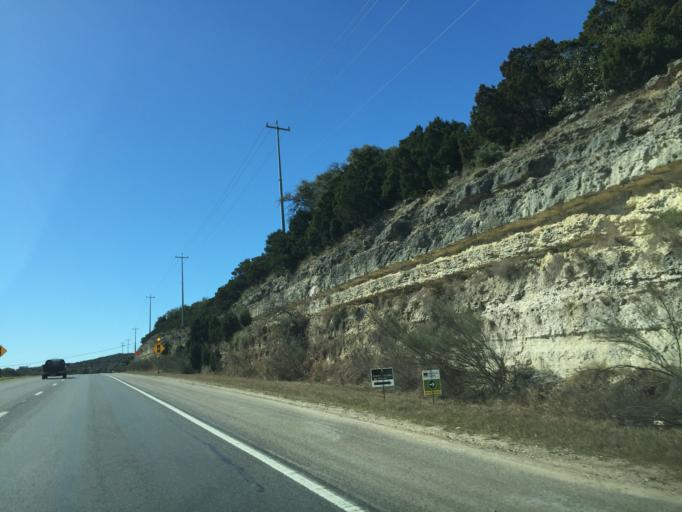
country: US
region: Texas
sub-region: Comal County
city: Bulverde
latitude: 29.7134
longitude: -98.4471
